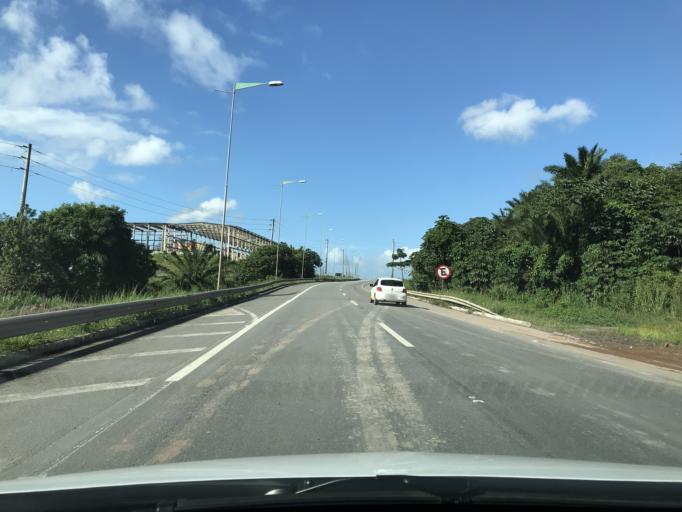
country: BR
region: Pernambuco
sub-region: Ipojuca
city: Ipojuca
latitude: -8.3693
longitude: -35.0086
